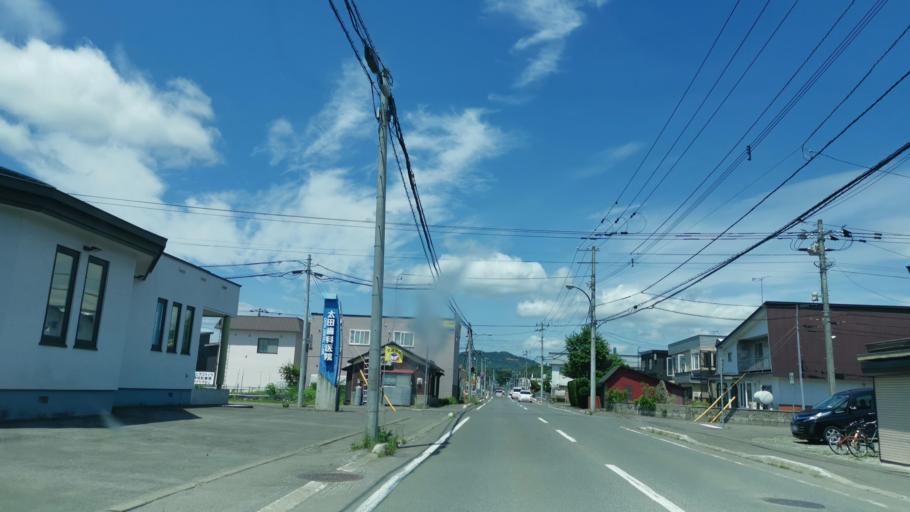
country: JP
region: Hokkaido
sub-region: Asahikawa-shi
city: Asahikawa
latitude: 43.7916
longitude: 142.3365
